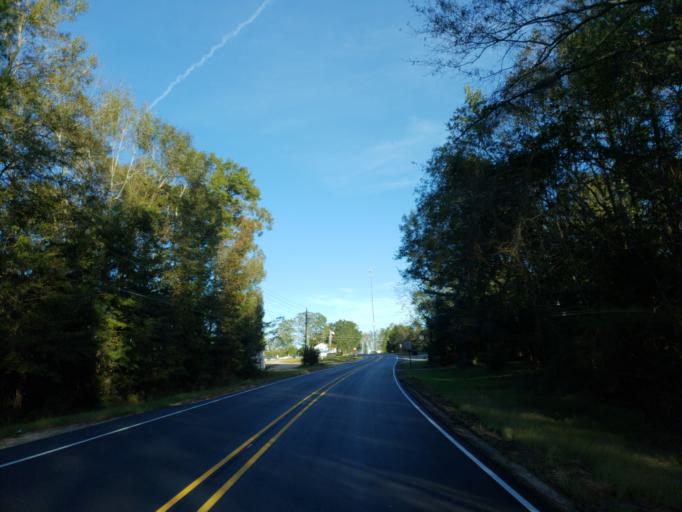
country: US
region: Mississippi
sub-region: Perry County
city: Richton
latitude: 31.3469
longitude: -88.7663
